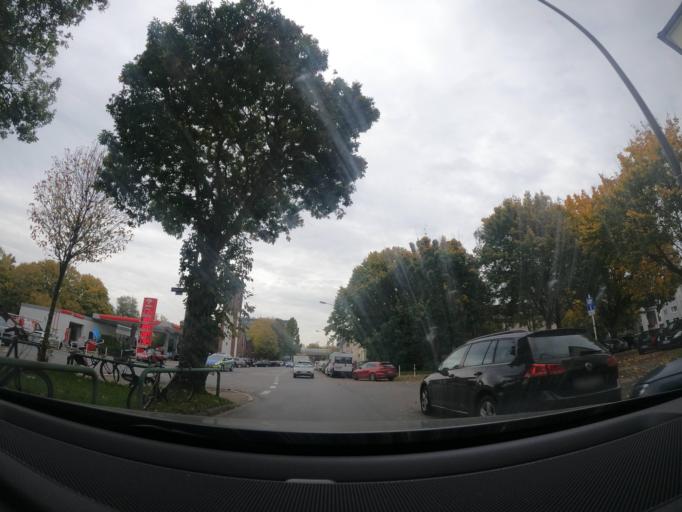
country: DE
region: North Rhine-Westphalia
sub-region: Regierungsbezirk Arnsberg
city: Dortmund
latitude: 51.5012
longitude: 7.4648
